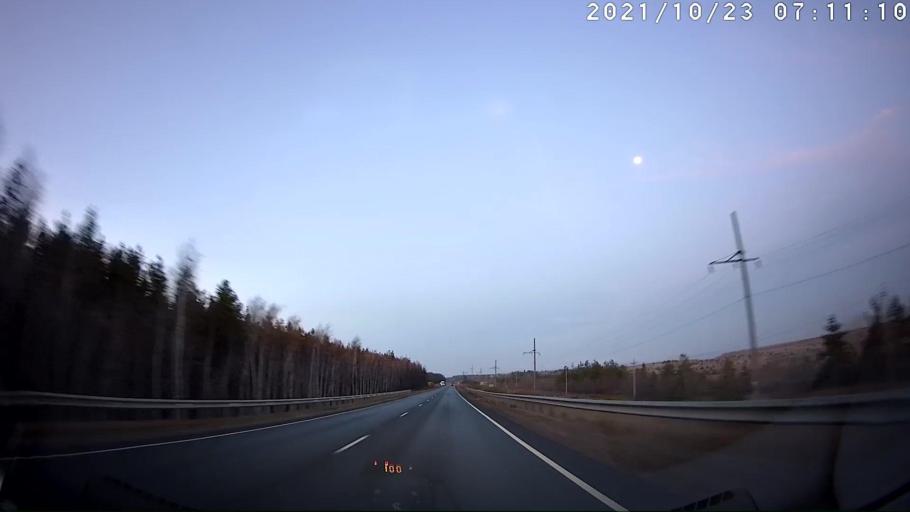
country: RU
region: Saratov
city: Khvalynsk
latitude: 52.5404
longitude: 48.0551
